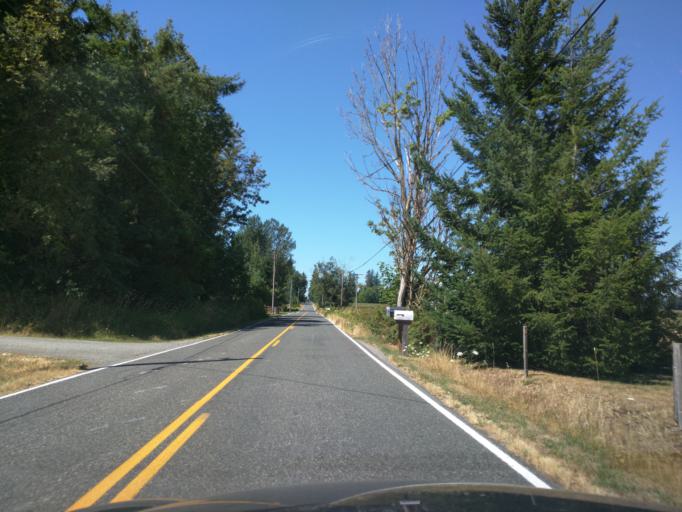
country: US
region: Washington
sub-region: Whatcom County
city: Lynden
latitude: 48.8772
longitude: -122.4201
